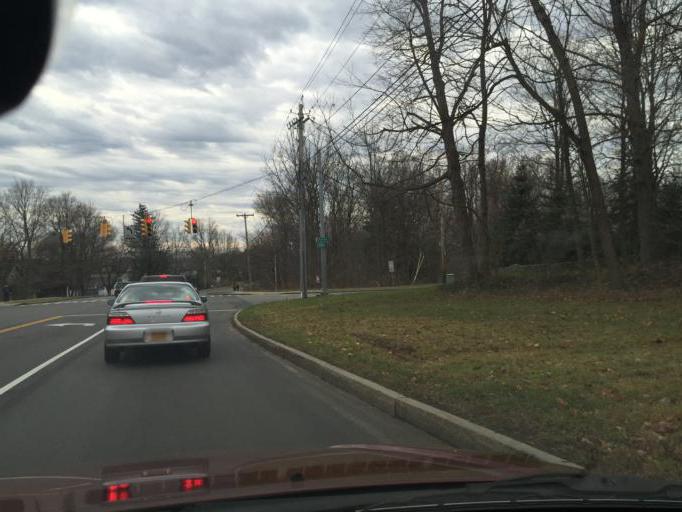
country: US
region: New York
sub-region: Monroe County
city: Rochester
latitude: 43.1323
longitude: -77.5902
